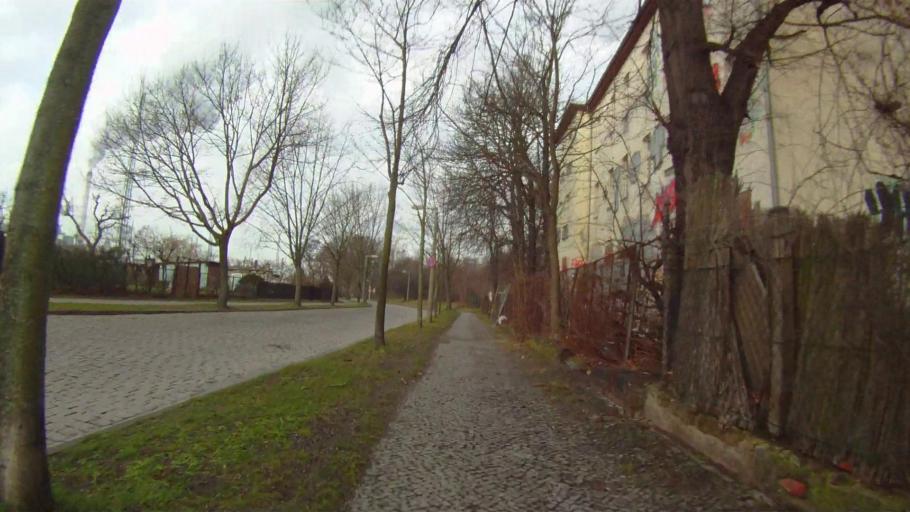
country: DE
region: Berlin
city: Friedrichsfelde
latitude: 52.4905
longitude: 13.5078
